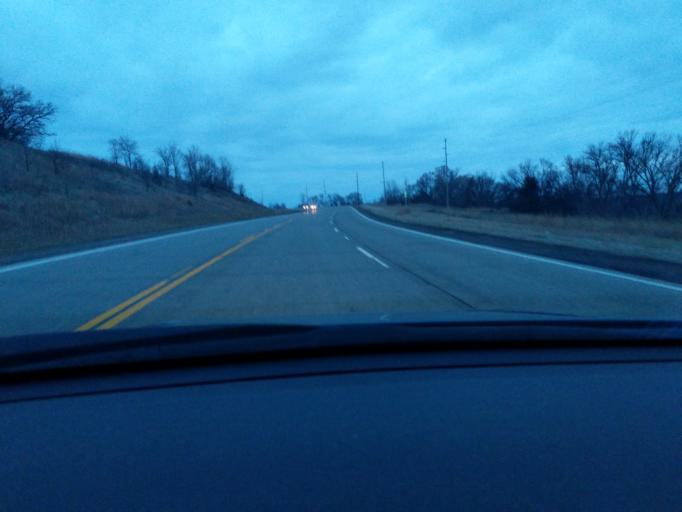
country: US
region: Minnesota
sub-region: Yellow Medicine County
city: Granite Falls
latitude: 44.8001
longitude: -95.5099
